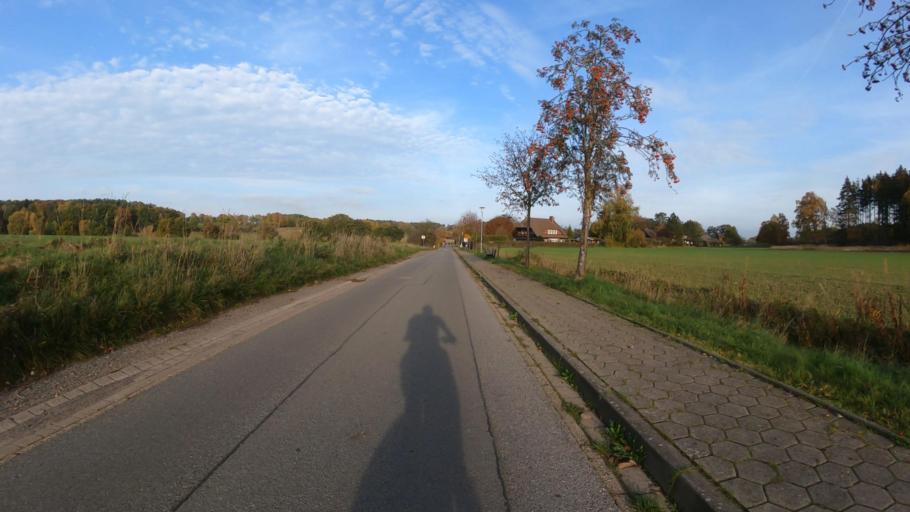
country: DE
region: Lower Saxony
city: Harmstorf
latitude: 53.3446
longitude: 9.9768
